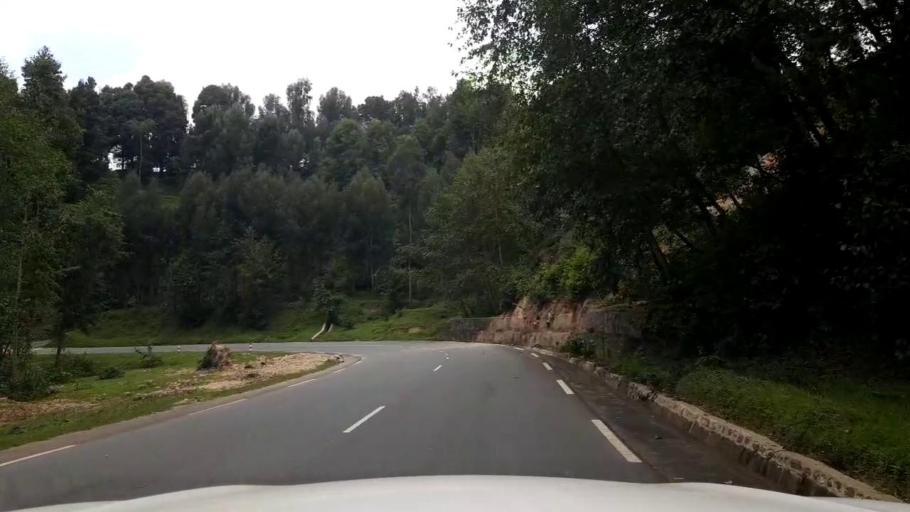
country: RW
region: Northern Province
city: Musanze
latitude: -1.6580
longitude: 29.5103
